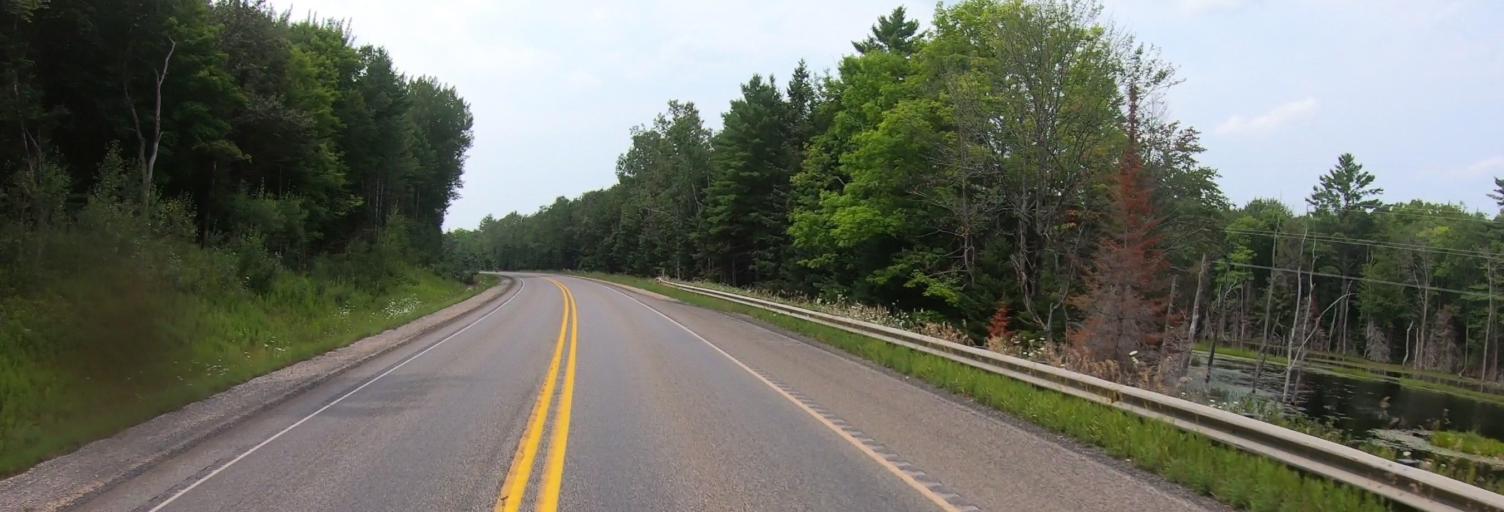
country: US
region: Michigan
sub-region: Alger County
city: Munising
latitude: 46.3336
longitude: -86.8299
